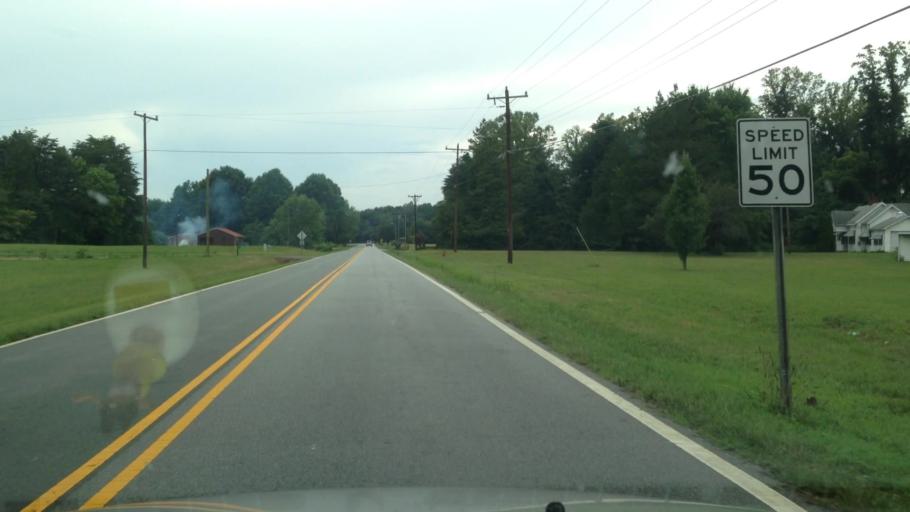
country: US
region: North Carolina
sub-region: Forsyth County
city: Walkertown
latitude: 36.1588
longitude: -80.1181
